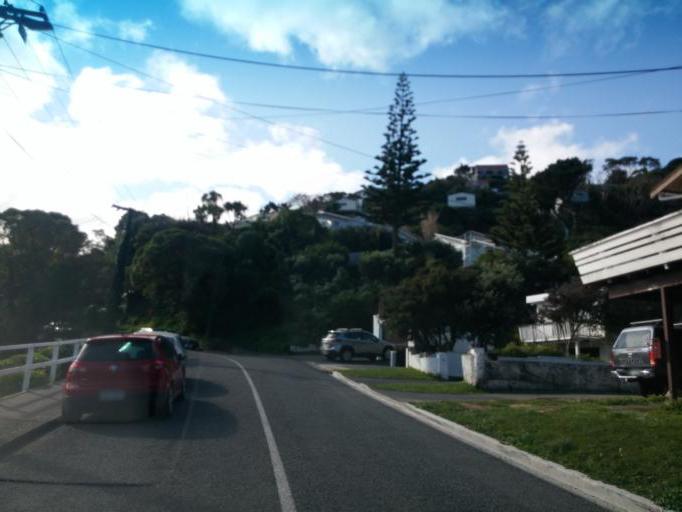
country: NZ
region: Wellington
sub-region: Wellington City
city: Wellington
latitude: -41.3214
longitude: 174.8213
